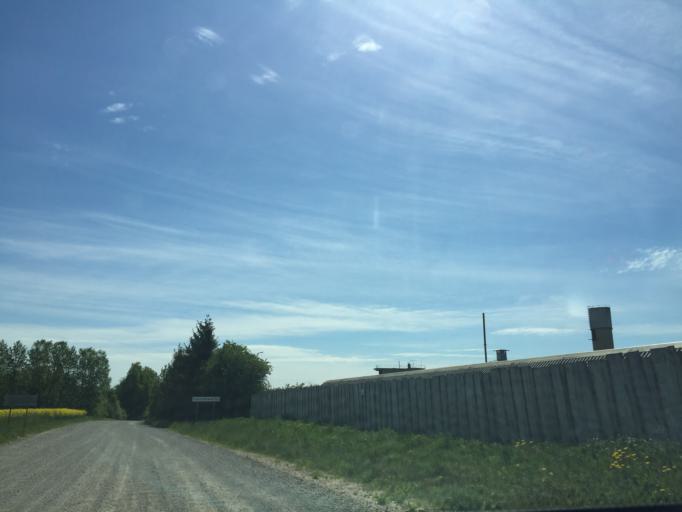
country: LT
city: Linkuva
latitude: 56.0713
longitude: 24.0728
